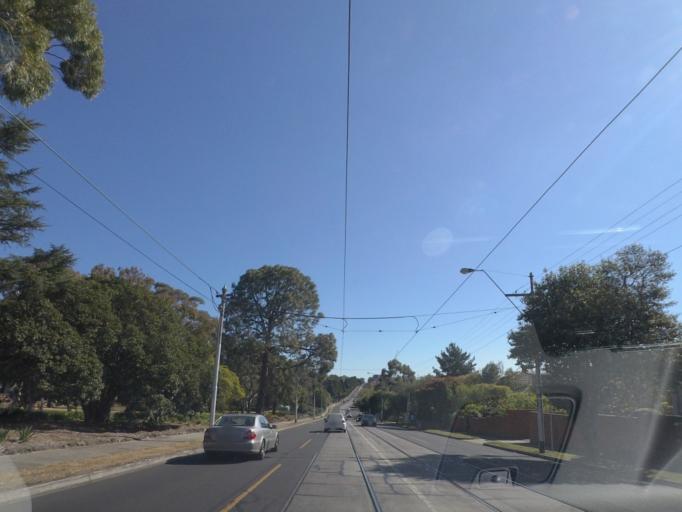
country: AU
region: Victoria
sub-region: Boroondara
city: Kew East
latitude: -37.8000
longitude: 145.0491
